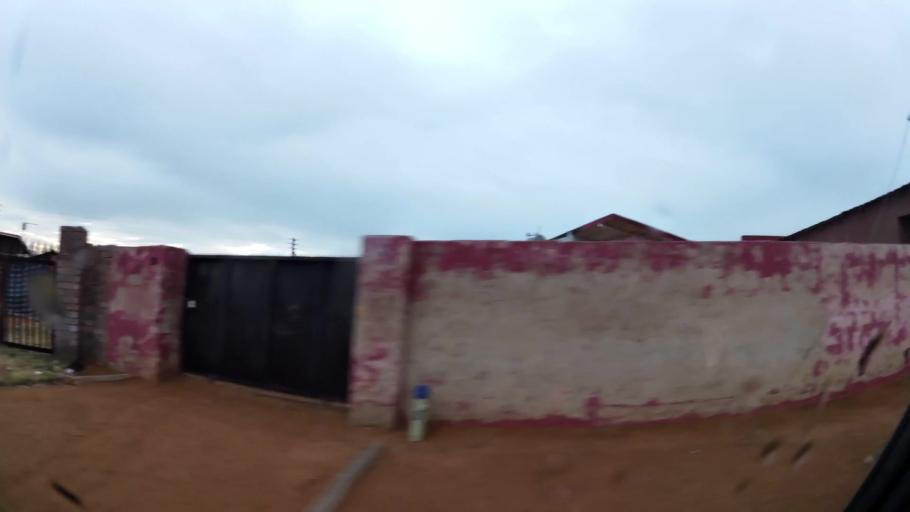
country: ZA
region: Gauteng
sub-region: City of Johannesburg Metropolitan Municipality
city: Roodepoort
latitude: -26.1725
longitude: 27.7911
